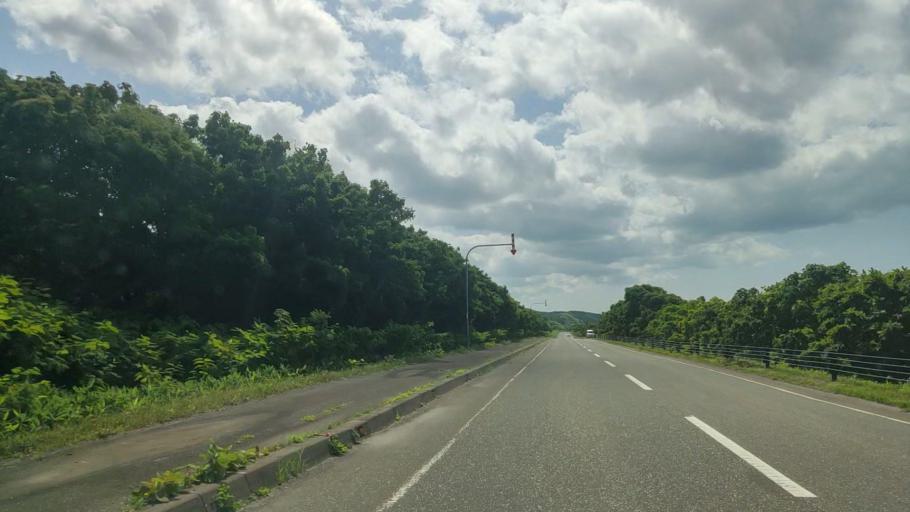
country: JP
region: Hokkaido
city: Wakkanai
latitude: 45.3591
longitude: 141.6617
